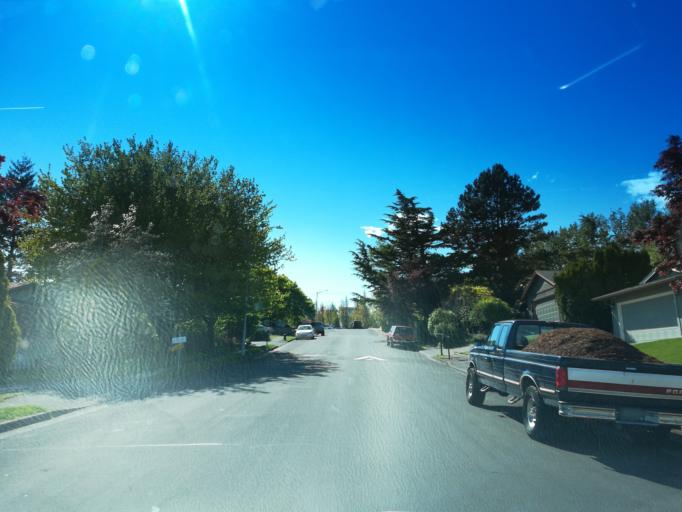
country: US
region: Oregon
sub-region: Multnomah County
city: Troutdale
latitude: 45.5309
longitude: -122.3860
